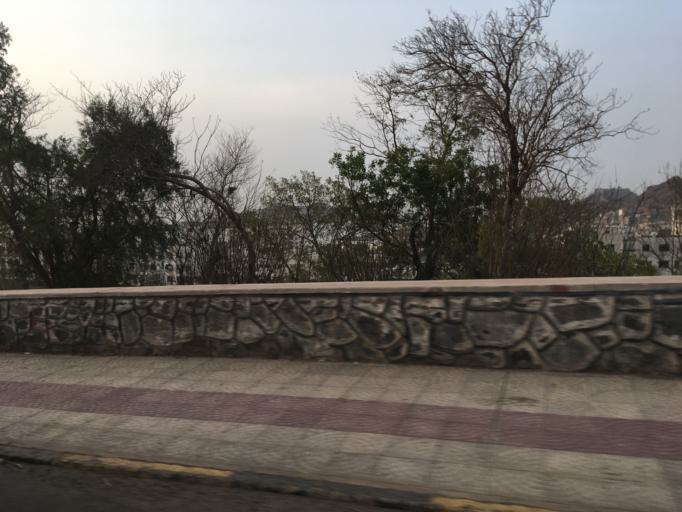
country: YE
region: Aden
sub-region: Craiter
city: Crater
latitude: 12.7887
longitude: 45.0225
